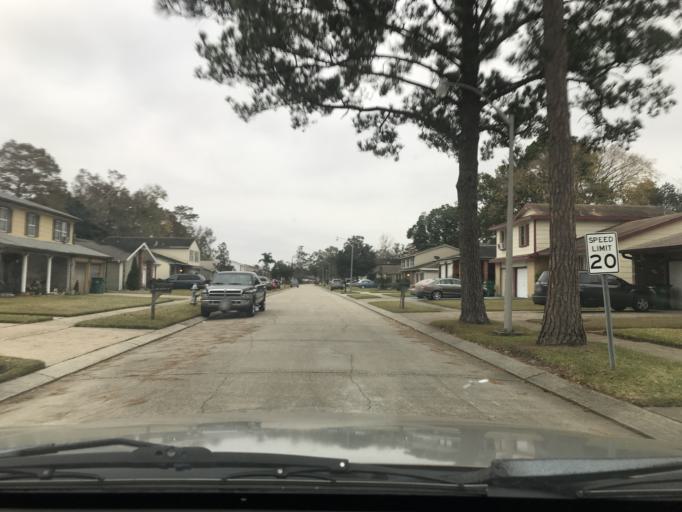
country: US
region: Louisiana
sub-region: Jefferson Parish
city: Woodmere
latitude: 29.8656
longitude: -90.0798
